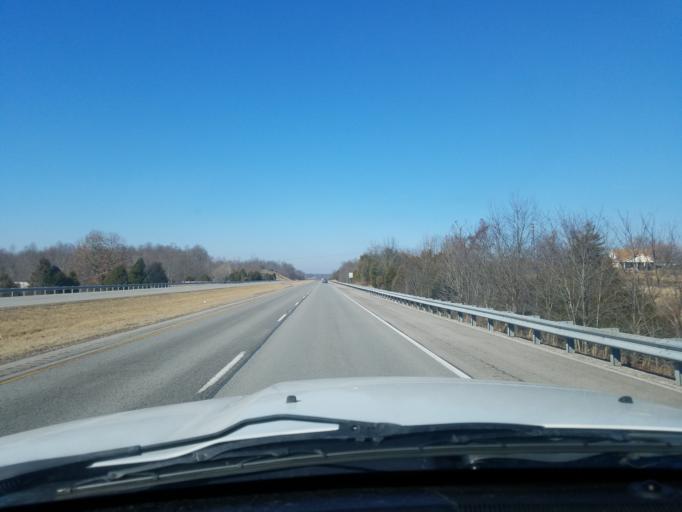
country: US
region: Kentucky
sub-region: Hardin County
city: Elizabethtown
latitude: 37.6318
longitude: -85.8245
